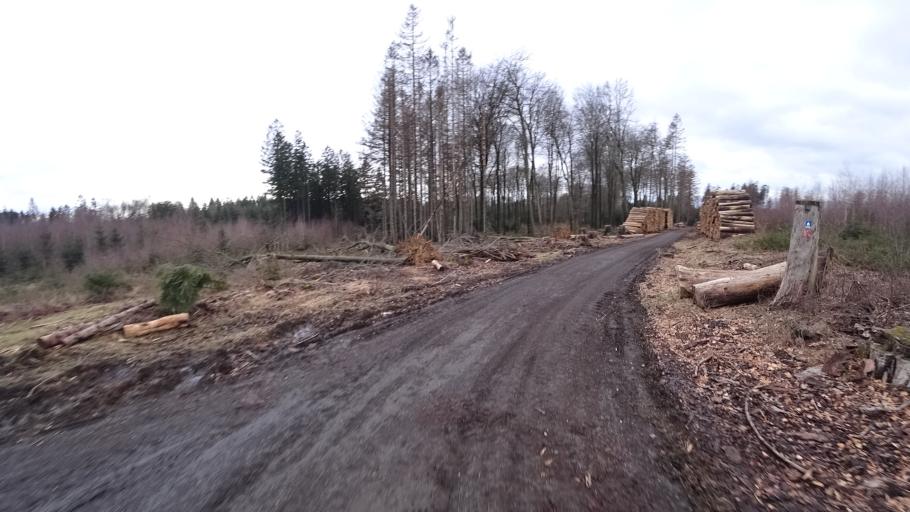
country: DE
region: Rheinland-Pfalz
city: Hillscheid
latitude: 50.4231
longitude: 7.7277
